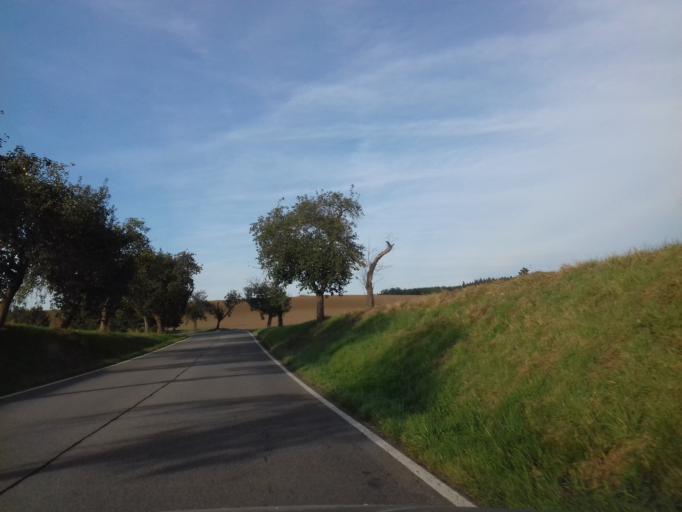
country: CZ
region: Central Bohemia
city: Kamenny Privoz
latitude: 49.8682
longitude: 14.5044
